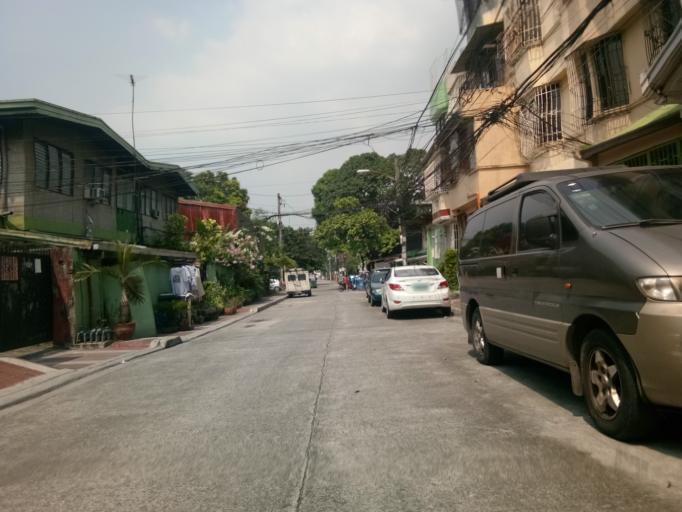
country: PH
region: Metro Manila
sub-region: Marikina
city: Calumpang
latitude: 14.6177
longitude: 121.0613
